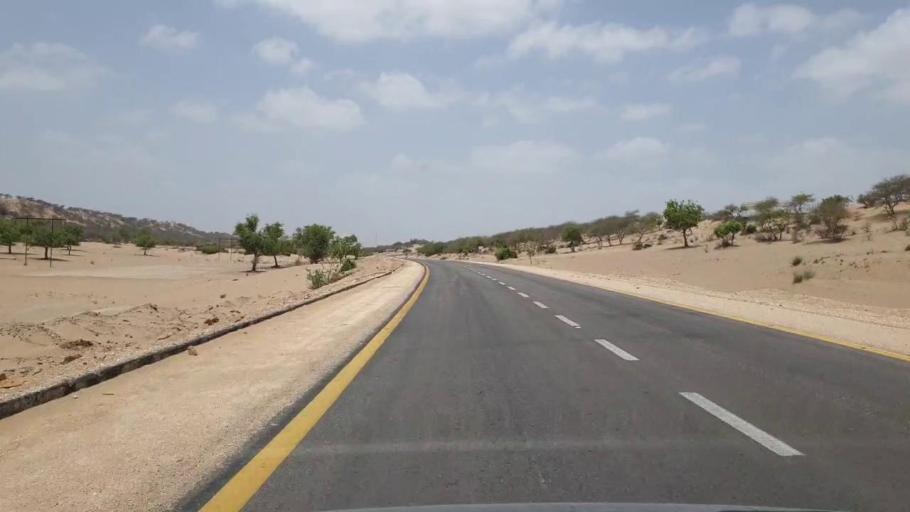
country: PK
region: Sindh
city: Mithi
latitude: 24.8380
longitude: 69.6411
